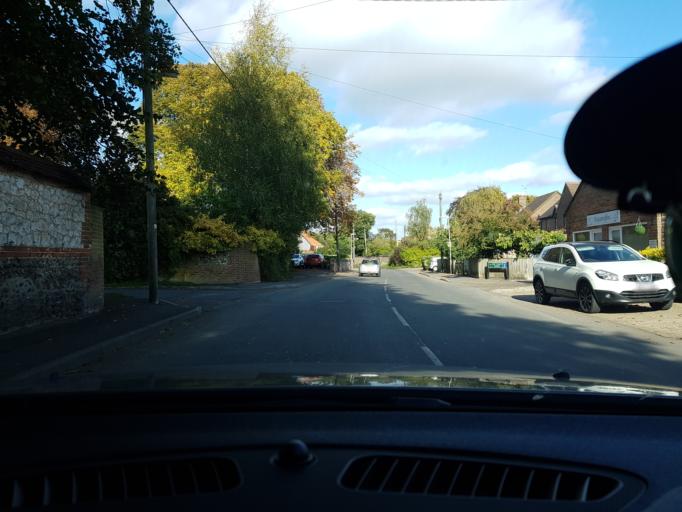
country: GB
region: England
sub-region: West Berkshire
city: Lambourn
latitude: 51.5079
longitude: -1.5346
